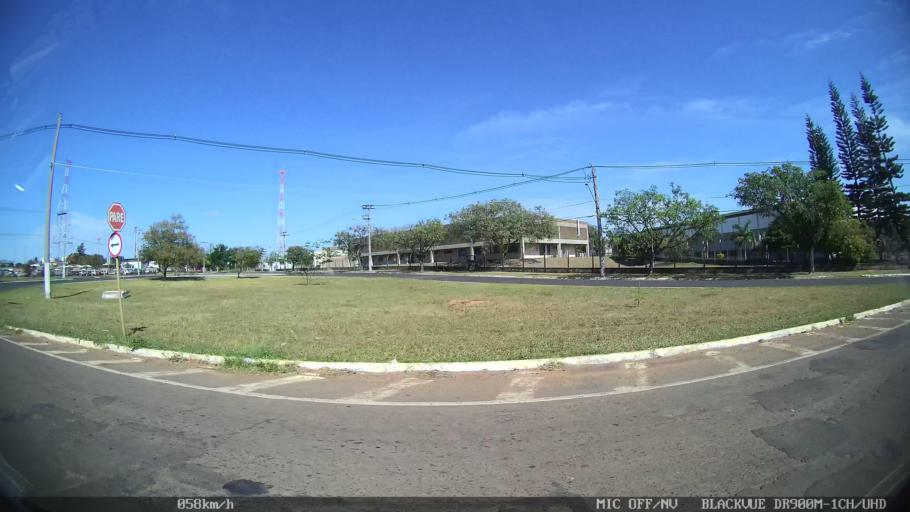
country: BR
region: Sao Paulo
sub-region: Franca
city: Franca
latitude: -20.5497
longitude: -47.4437
